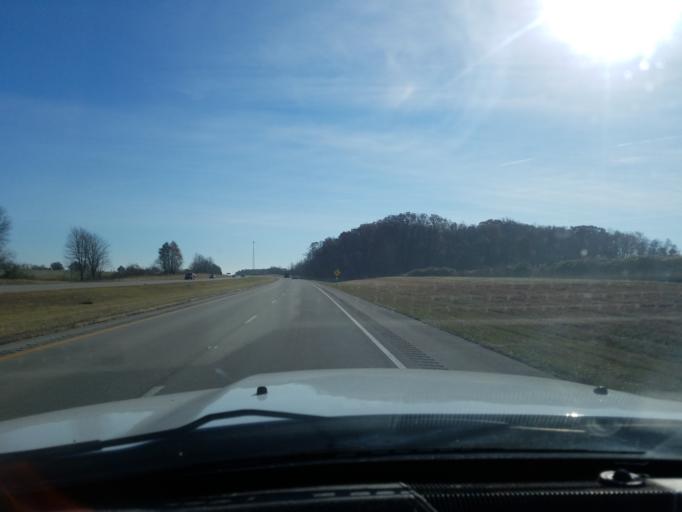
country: US
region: Ohio
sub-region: Adams County
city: Winchester
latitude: 38.9725
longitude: -83.7389
